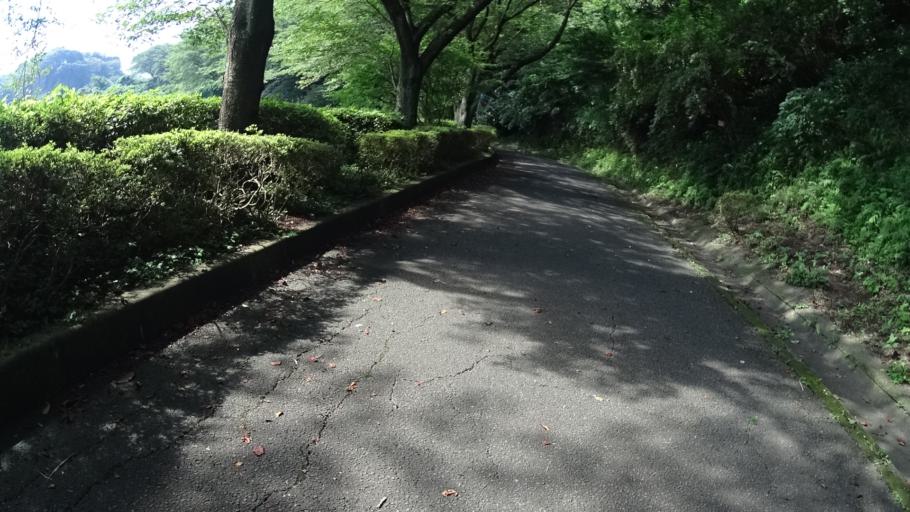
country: JP
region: Kanagawa
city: Zushi
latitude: 35.3086
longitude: 139.6127
